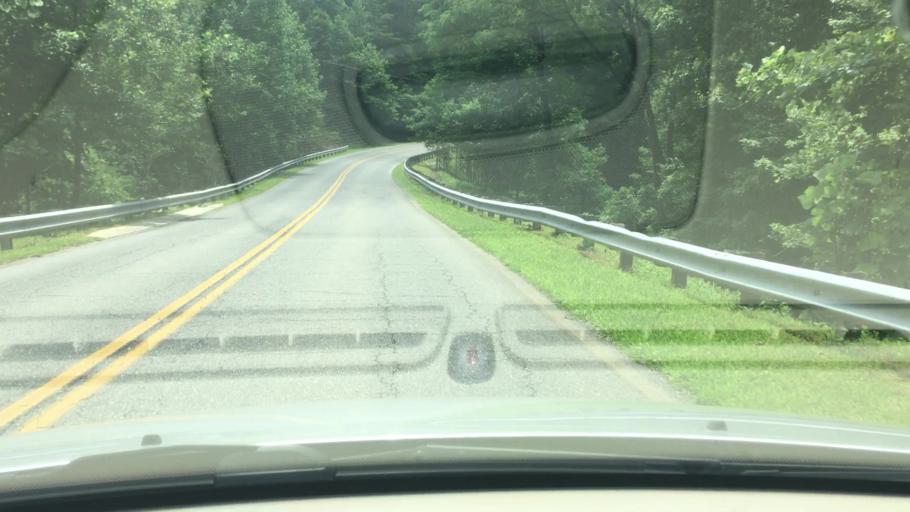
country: US
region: Georgia
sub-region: Dawson County
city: Dawsonville
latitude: 34.5609
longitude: -84.2535
